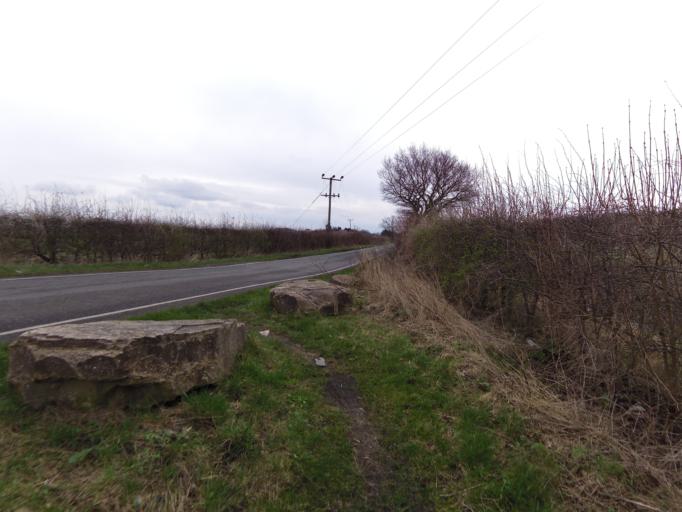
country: GB
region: England
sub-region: Doncaster
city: Bentley
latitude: 53.5703
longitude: -1.1380
